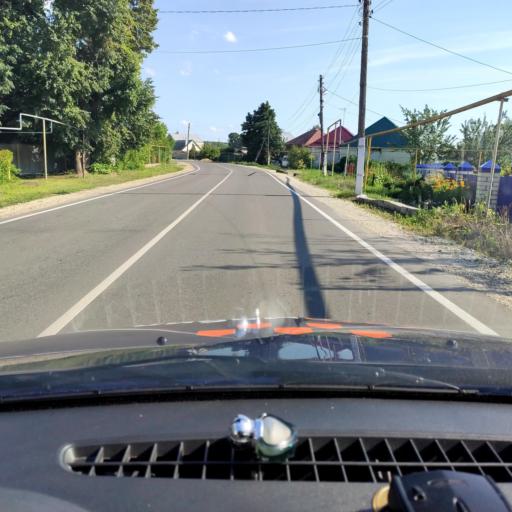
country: RU
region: Voronezj
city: Devitsa
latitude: 51.6561
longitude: 38.9704
